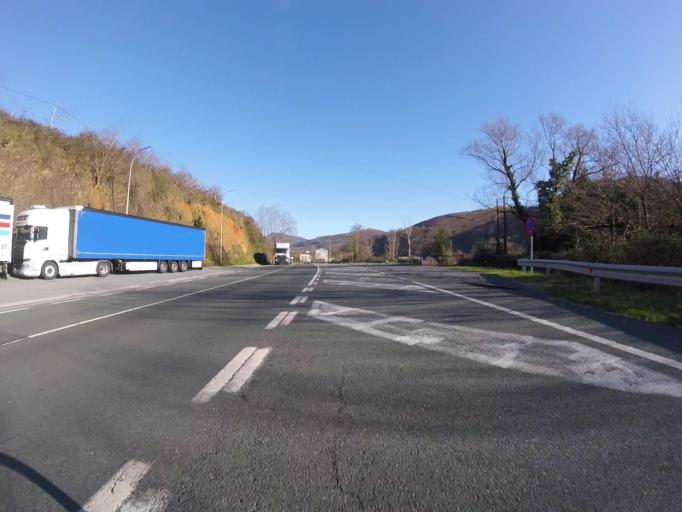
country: ES
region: Navarre
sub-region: Provincia de Navarra
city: Bera
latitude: 43.2777
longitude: -1.7080
